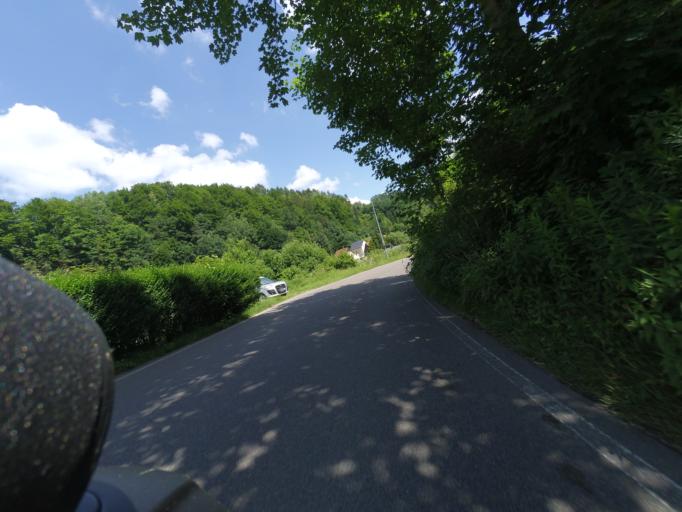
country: DE
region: Saxony
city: Porschdorf
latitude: 50.9374
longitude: 14.1278
